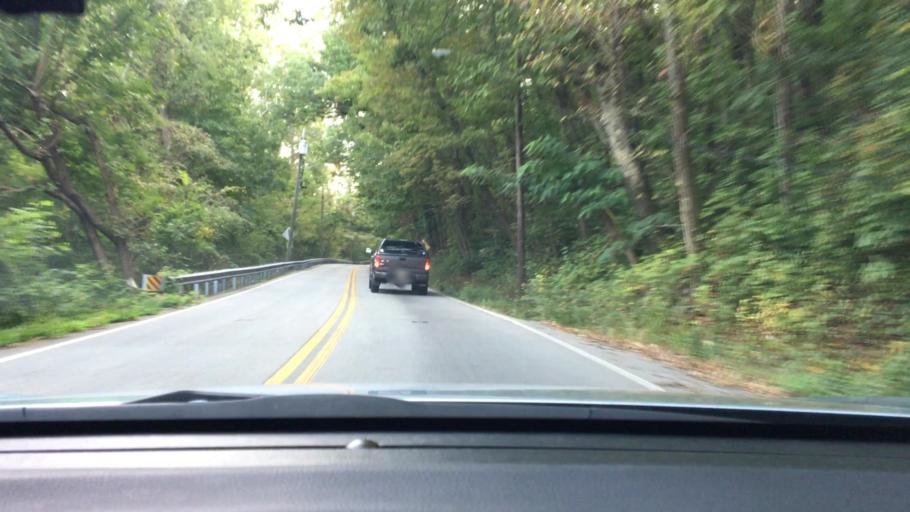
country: US
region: Tennessee
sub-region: Hamilton County
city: Lookout Mountain
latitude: 35.0035
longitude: -85.3327
